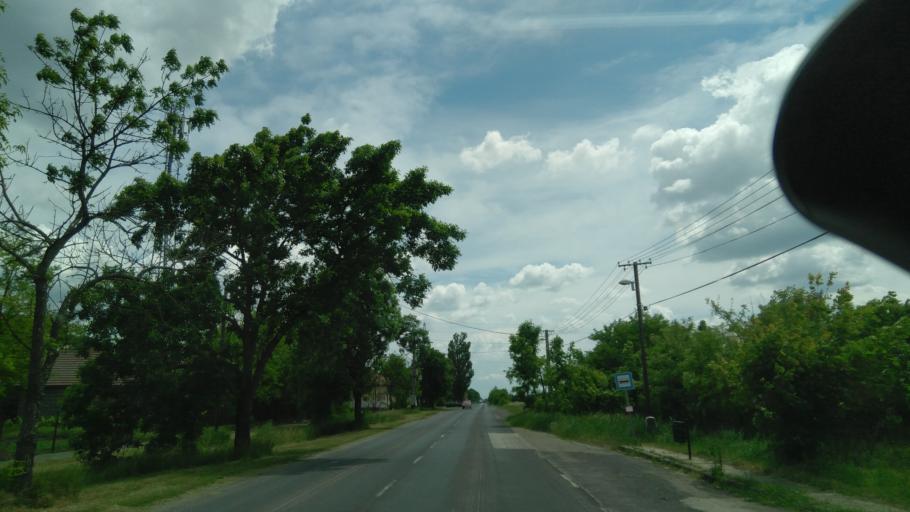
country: HU
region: Bekes
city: Oroshaza
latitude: 46.5415
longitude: 20.6772
